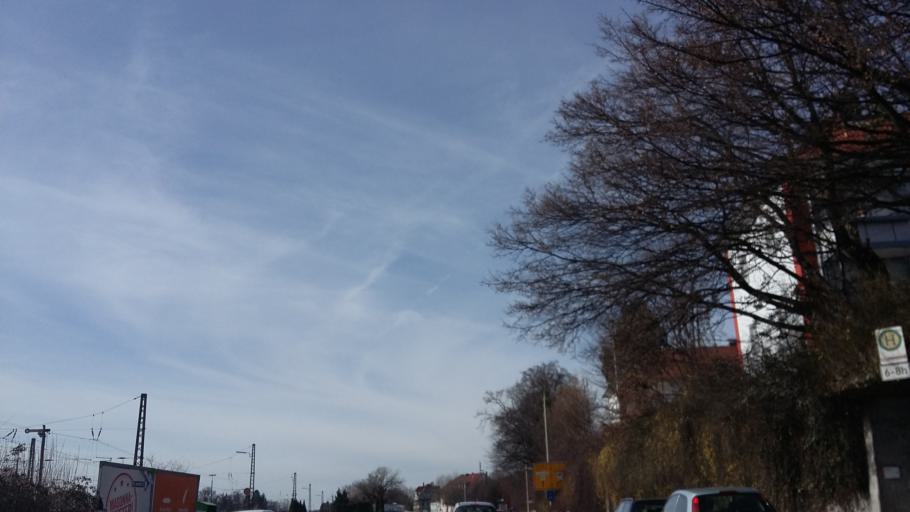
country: DE
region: Bavaria
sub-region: Swabia
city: Lindau
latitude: 47.5527
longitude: 9.7089
